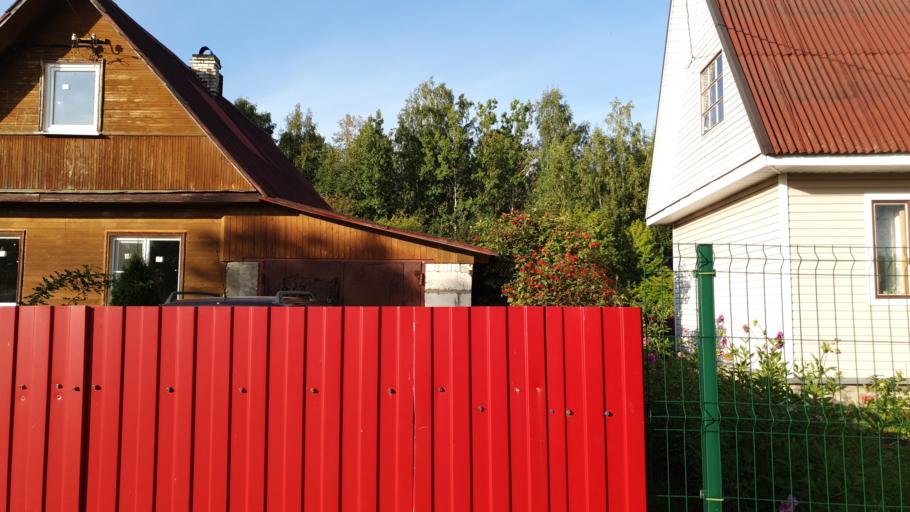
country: RU
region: Leningrad
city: Ivangorod
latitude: 59.4230
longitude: 28.3353
